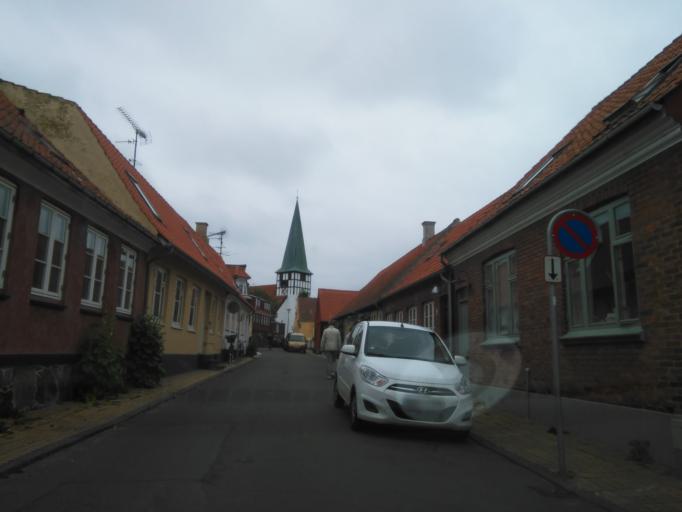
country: DK
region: Capital Region
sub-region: Bornholm Kommune
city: Ronne
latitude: 55.0999
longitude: 14.6959
